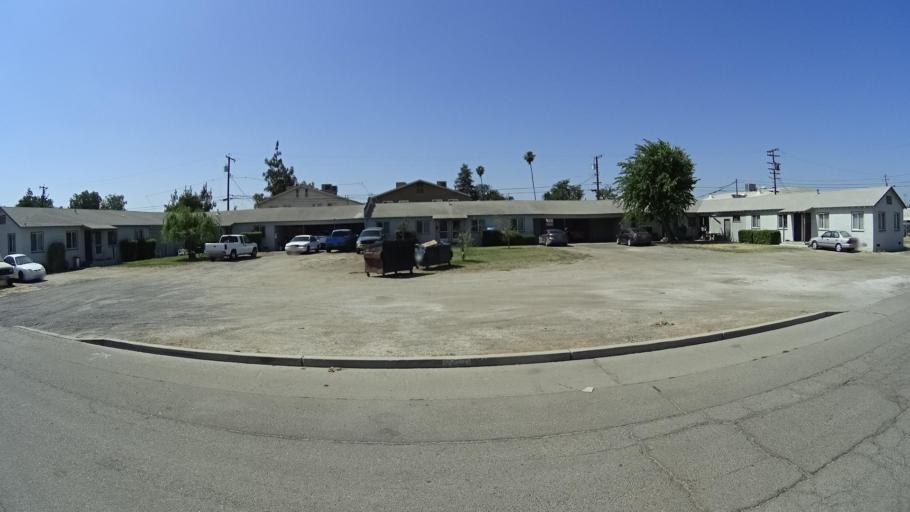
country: US
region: California
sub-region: Fresno County
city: Fresno
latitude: 36.7596
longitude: -119.7787
